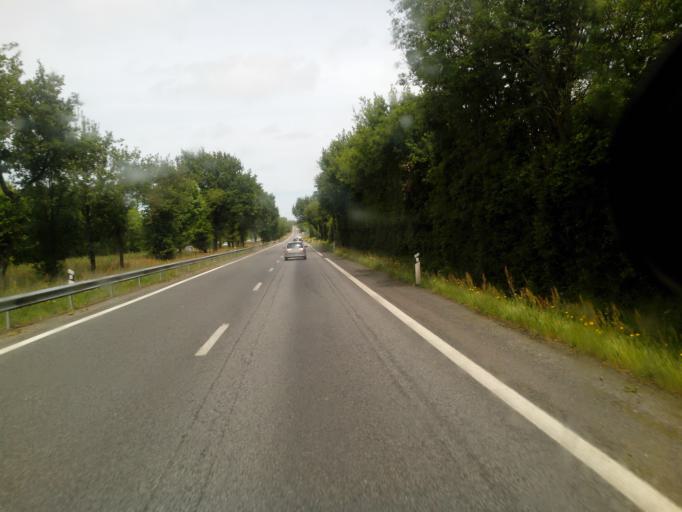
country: FR
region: Brittany
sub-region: Departement d'Ille-et-Vilaine
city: Grand-Fougeray
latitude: 47.7099
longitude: -1.7052
